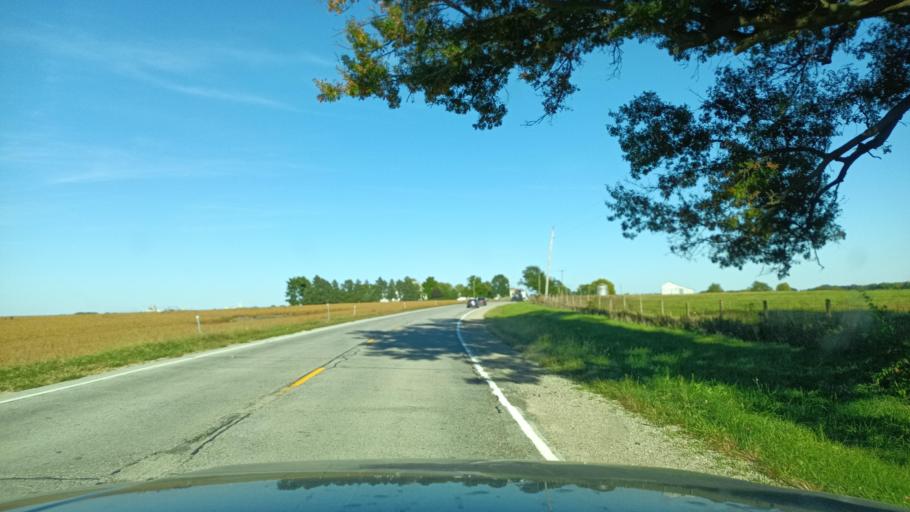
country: US
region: Illinois
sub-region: De Witt County
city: Farmer City
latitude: 40.2315
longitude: -88.6763
